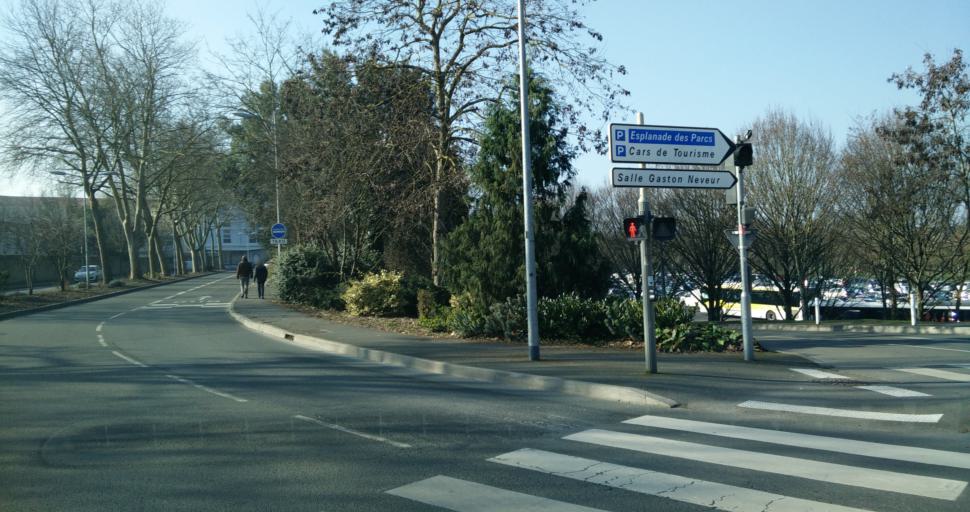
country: FR
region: Poitou-Charentes
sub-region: Departement de la Charente-Maritime
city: La Rochelle
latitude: 46.1665
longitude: -1.1532
